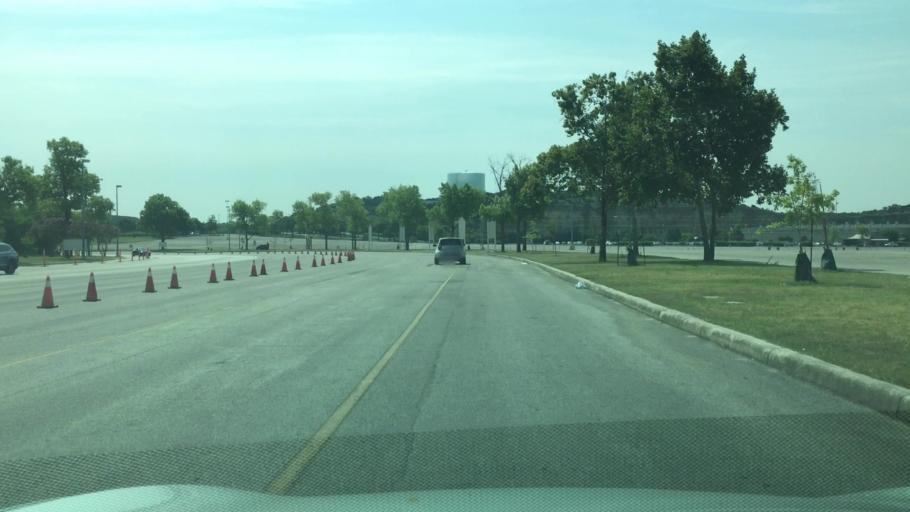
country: US
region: Texas
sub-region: Bexar County
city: Shavano Park
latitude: 29.6040
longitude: -98.6083
